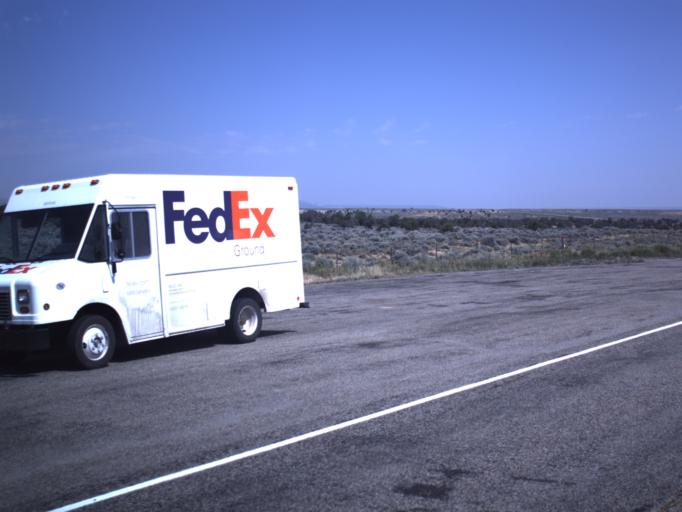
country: US
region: Utah
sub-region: Daggett County
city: Manila
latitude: 40.9978
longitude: -109.8419
